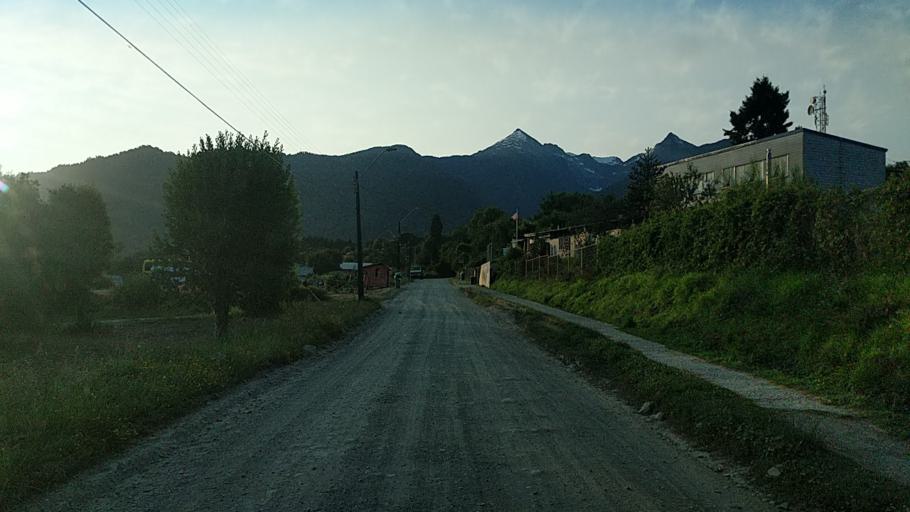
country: CL
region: Los Lagos
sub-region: Provincia de Llanquihue
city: La Ensenada
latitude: -41.4937
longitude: -72.3063
